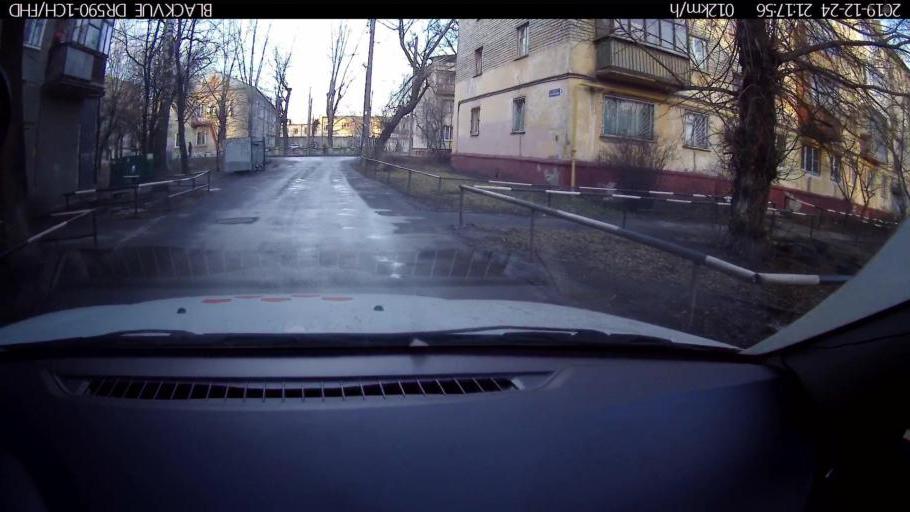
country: RU
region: Nizjnij Novgorod
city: Gorbatovka
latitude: 56.2649
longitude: 43.8780
